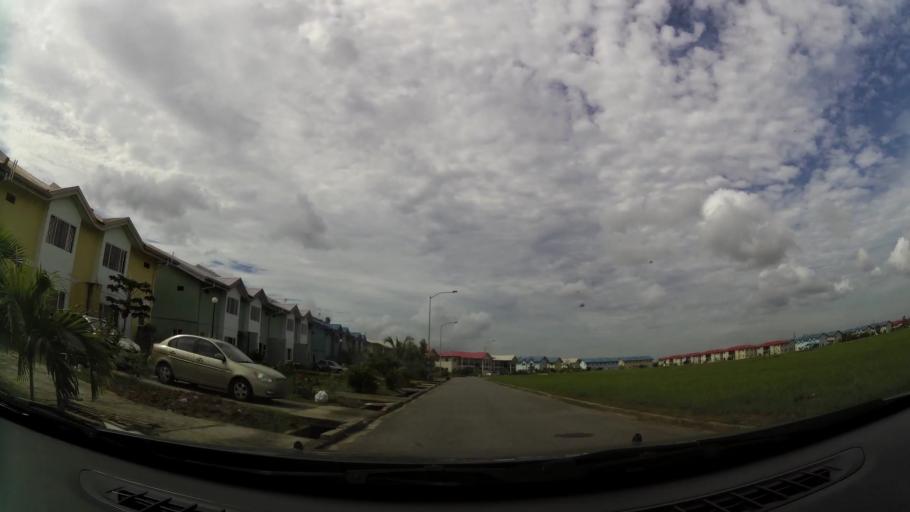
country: TT
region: Chaguanas
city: Chaguanas
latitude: 10.5039
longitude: -61.3968
